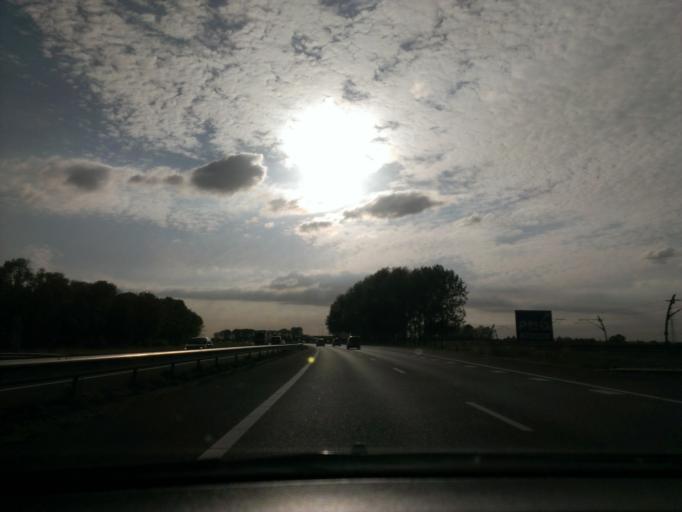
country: NL
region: Gelderland
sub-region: Gemeente Druten
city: Druten
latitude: 51.9232
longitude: 5.6143
